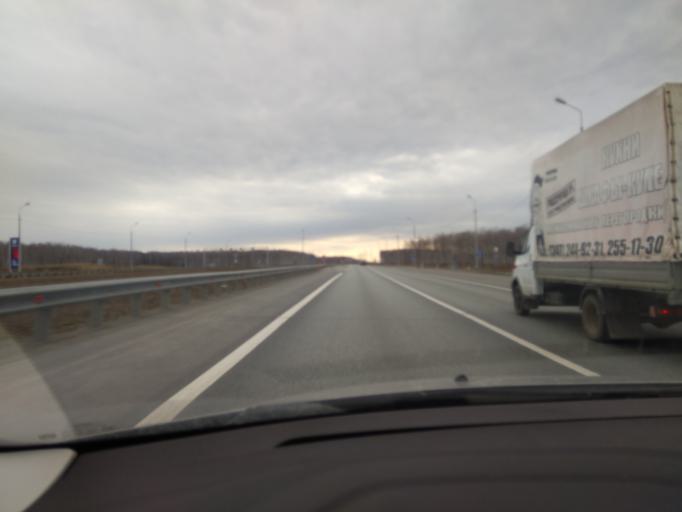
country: RU
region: Chelyabinsk
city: Chebarkul'
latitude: 54.9105
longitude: 60.4364
